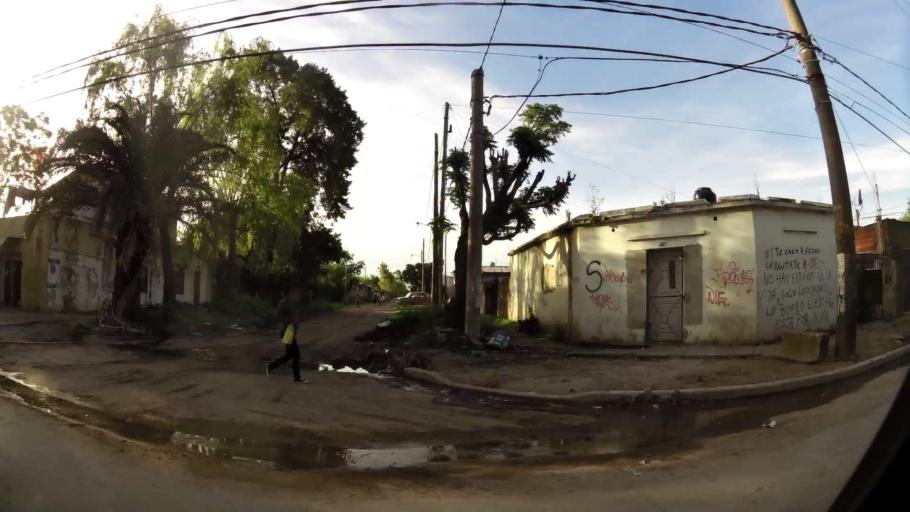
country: AR
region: Buenos Aires
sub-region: Partido de Almirante Brown
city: Adrogue
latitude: -34.7944
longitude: -58.3294
